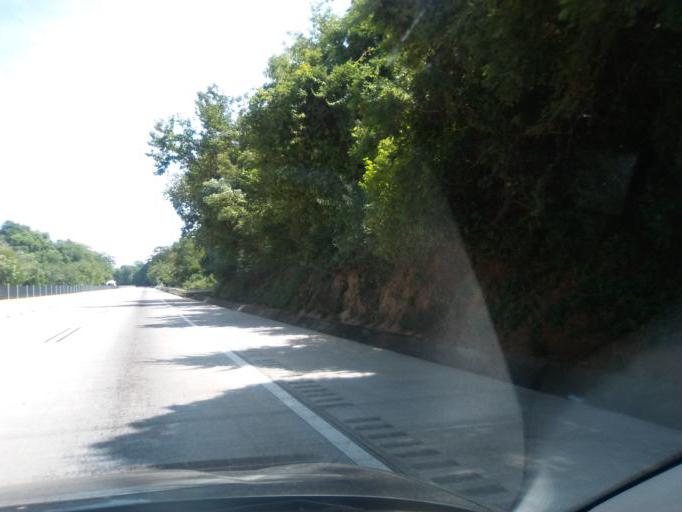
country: MX
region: Guerrero
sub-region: Acapulco de Juarez
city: Kilometro 30
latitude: 16.9508
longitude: -99.7601
